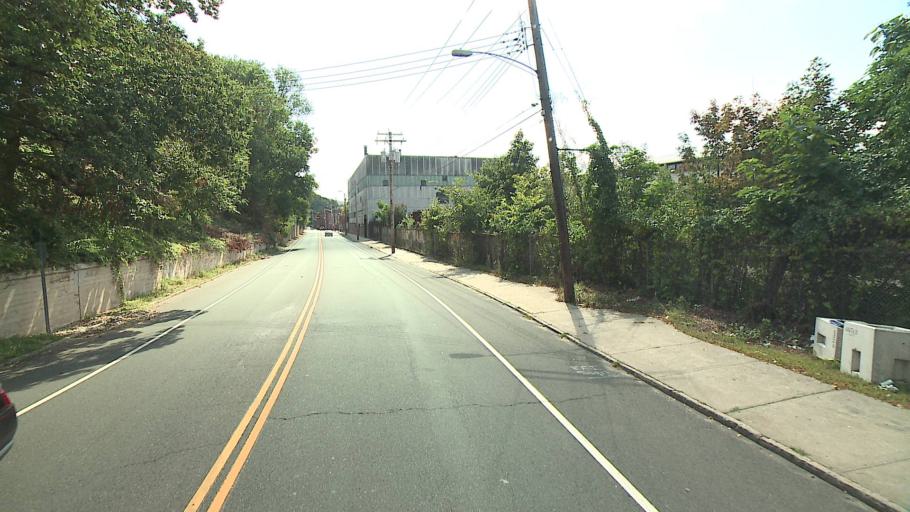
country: US
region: Connecticut
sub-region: New Haven County
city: Ansonia
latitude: 41.3486
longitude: -73.0804
